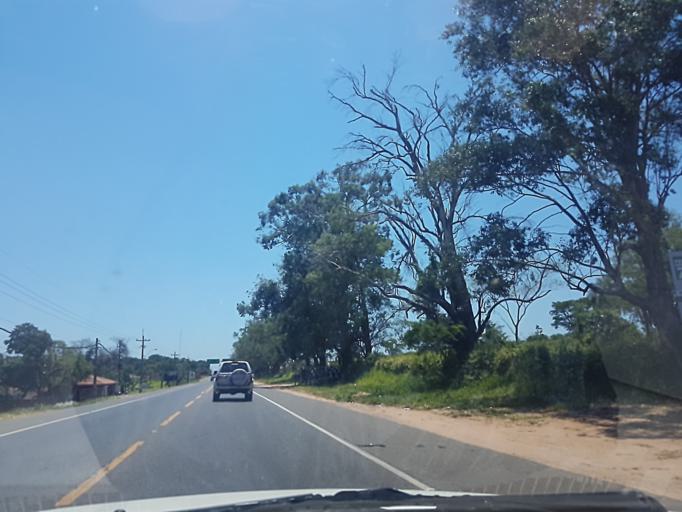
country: PY
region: Cordillera
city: Eusebio Ayala
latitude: -25.3844
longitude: -57.0525
